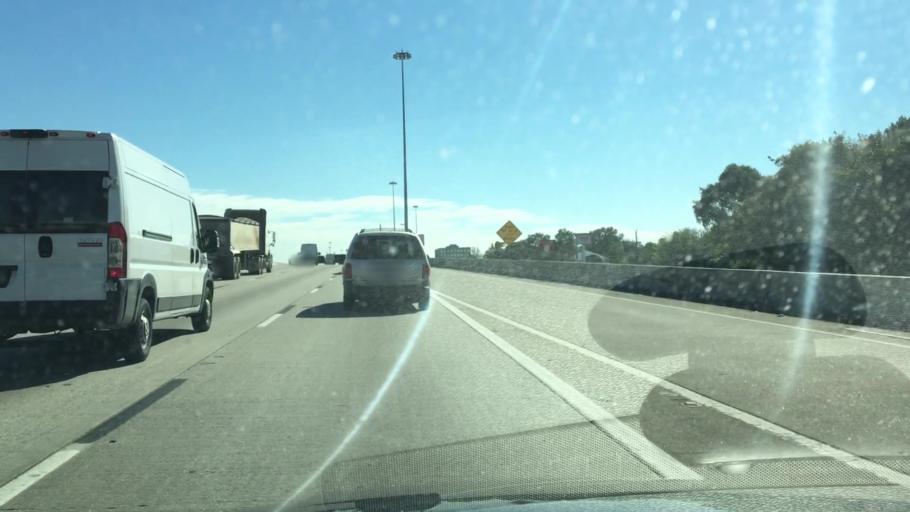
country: US
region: Texas
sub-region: Harris County
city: Houston
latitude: 29.8510
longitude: -95.3340
